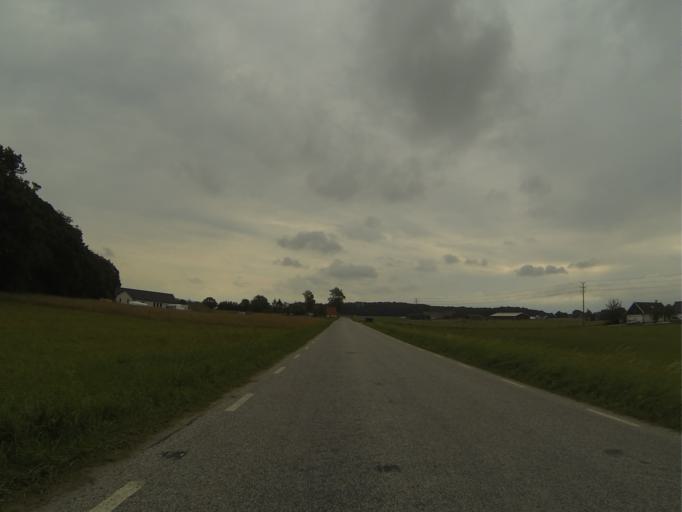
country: SE
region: Skane
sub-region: Lunds Kommun
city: Lund
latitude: 55.7303
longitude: 13.2985
